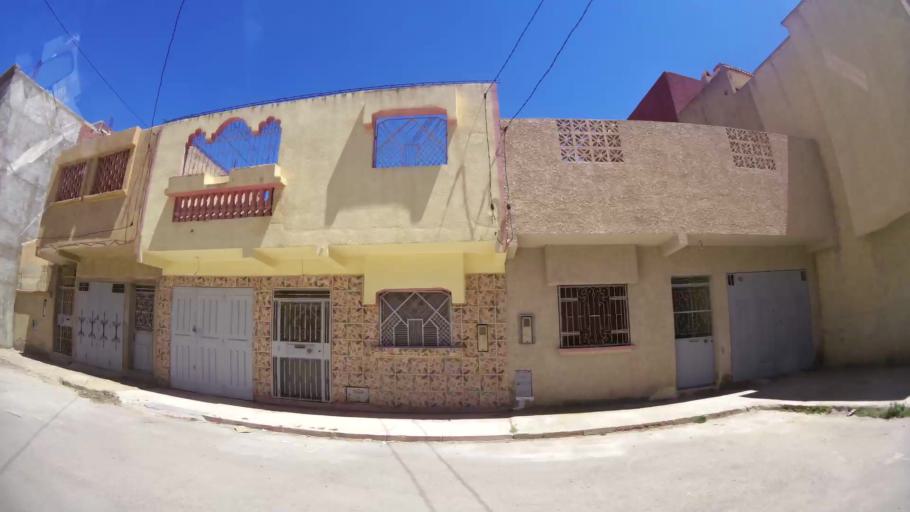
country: MA
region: Oriental
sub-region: Oujda-Angad
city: Oujda
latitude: 34.6719
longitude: -1.8913
